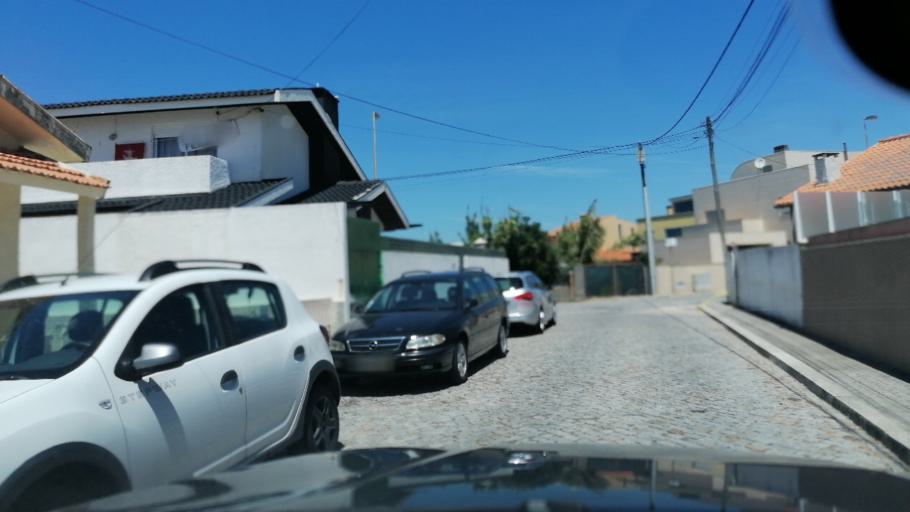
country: PT
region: Porto
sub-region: Matosinhos
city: Lavra
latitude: 41.2515
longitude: -8.7219
